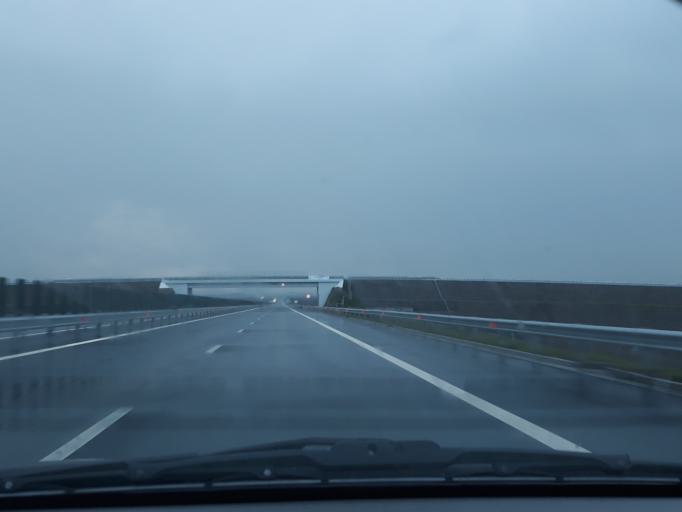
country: RO
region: Mures
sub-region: Comuna Ogra
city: Ogra
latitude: 46.4372
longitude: 24.3226
